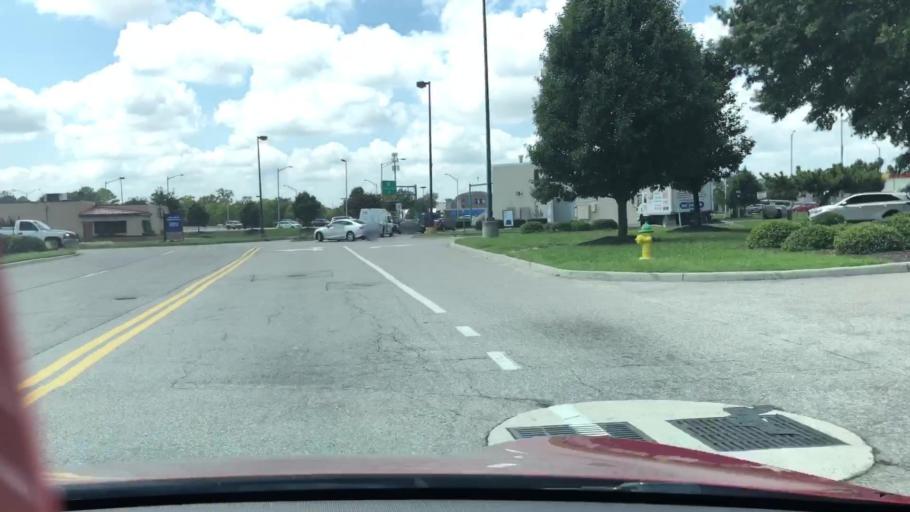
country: US
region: Virginia
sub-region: City of Chesapeake
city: Chesapeake
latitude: 36.8592
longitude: -76.2083
